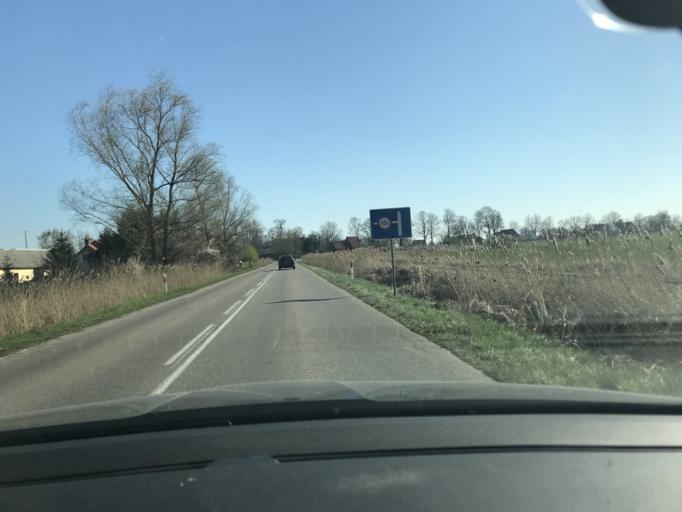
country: PL
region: Pomeranian Voivodeship
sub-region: Powiat nowodworski
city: Nowy Dwor Gdanski
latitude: 54.2450
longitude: 19.1418
